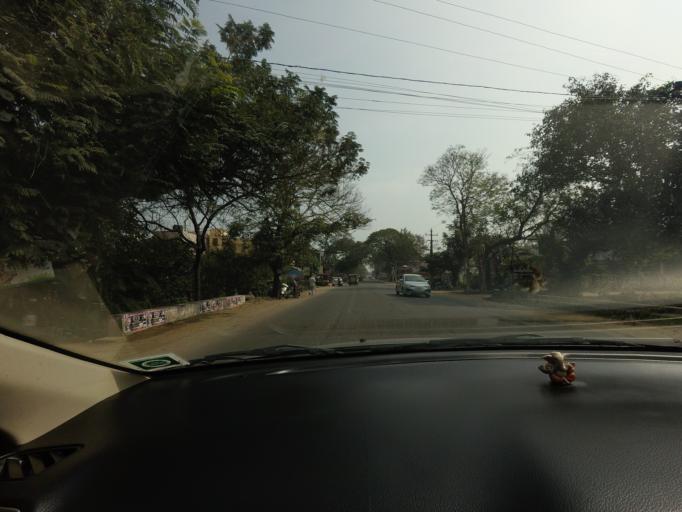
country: IN
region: Andhra Pradesh
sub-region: Krishna
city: Kankipadu
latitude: 16.4389
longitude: 80.7619
